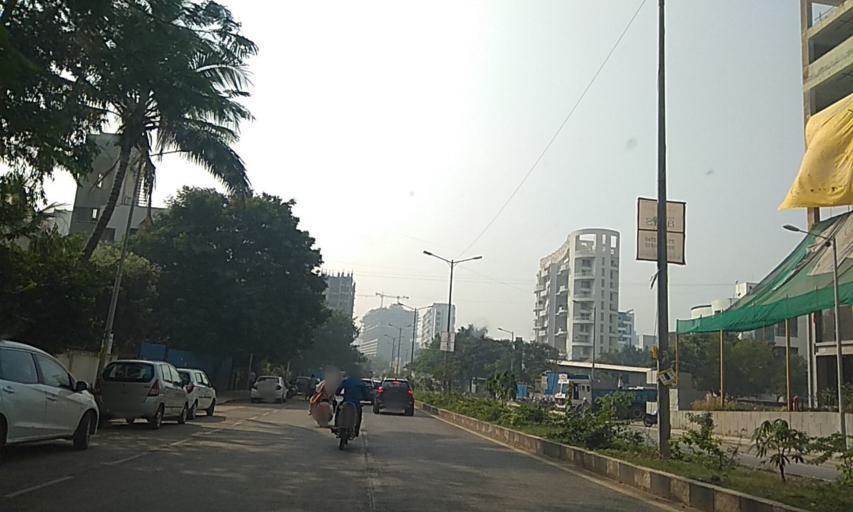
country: IN
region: Maharashtra
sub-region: Pune Division
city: Pimpri
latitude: 18.5633
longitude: 73.7768
